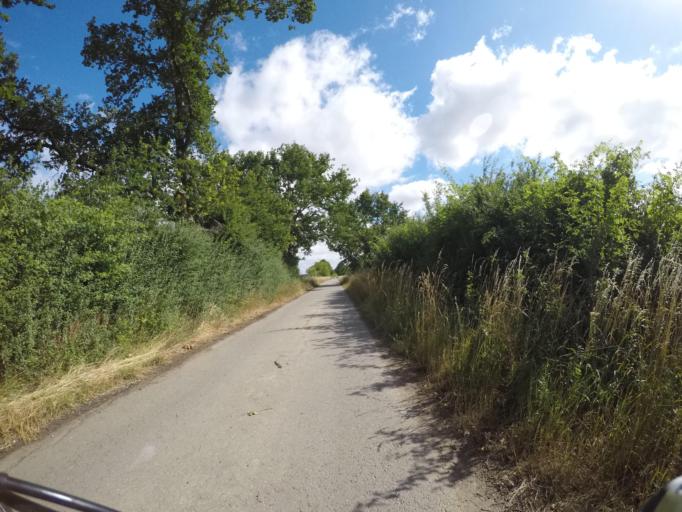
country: DE
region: Lower Saxony
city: Hitzacker
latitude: 53.1680
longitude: 11.0602
